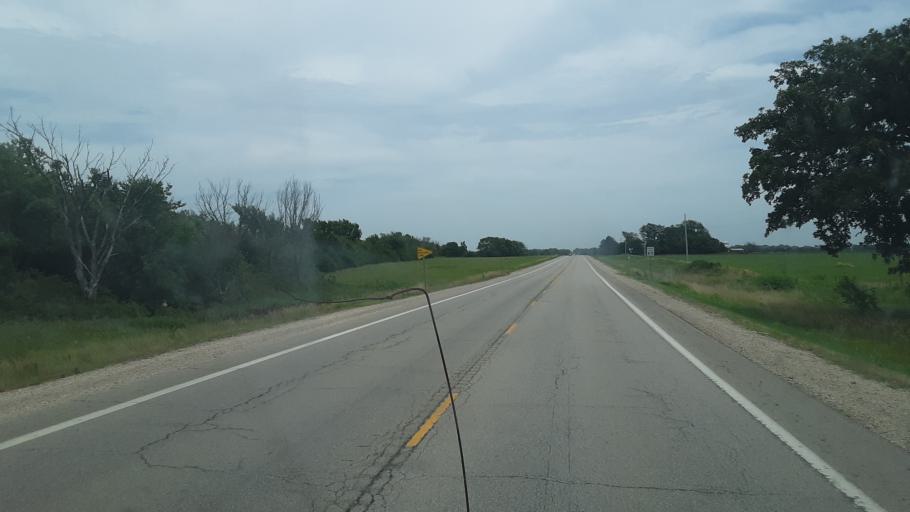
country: US
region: Kansas
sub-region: Woodson County
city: Yates Center
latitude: 37.8796
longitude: -95.7659
